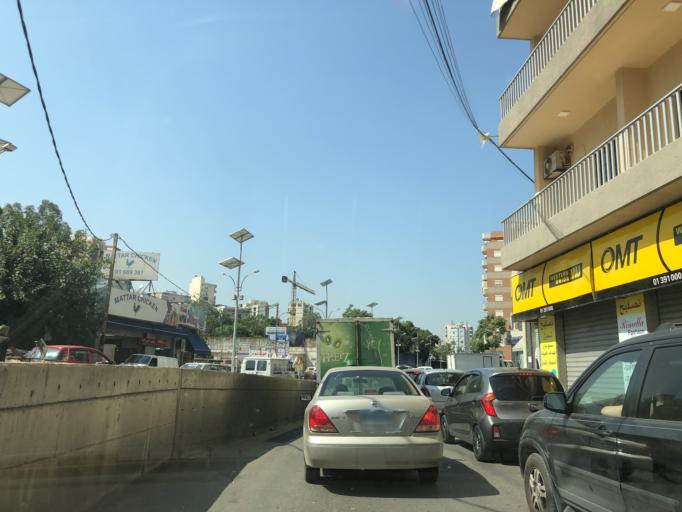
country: LB
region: Mont-Liban
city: Jdaidet el Matn
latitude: 33.8756
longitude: 35.5476
